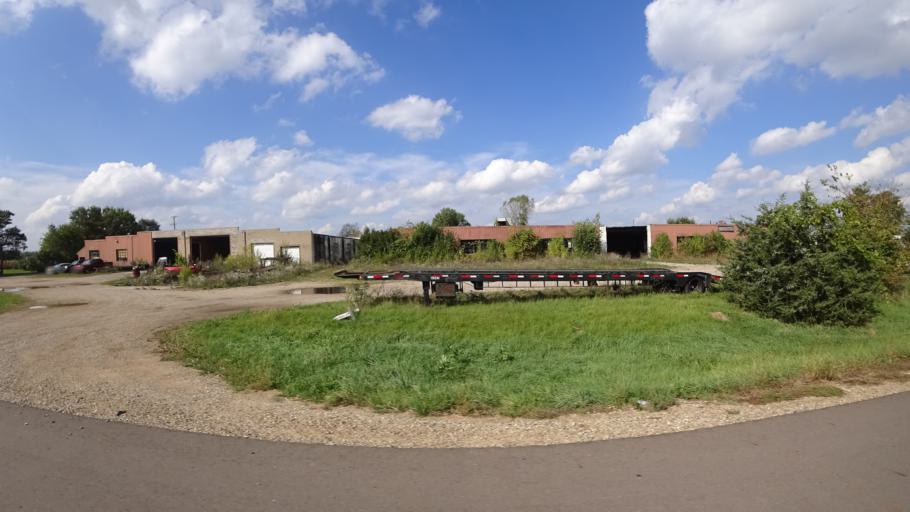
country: US
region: Michigan
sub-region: Branch County
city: Union City
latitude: 42.0750
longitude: -85.1392
